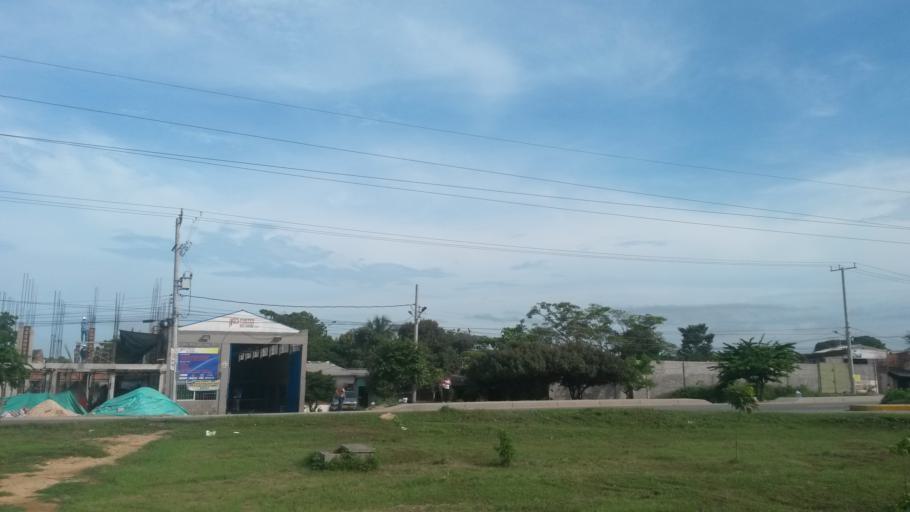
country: CO
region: Bolivar
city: Cartagena
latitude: 10.4049
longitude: -75.4546
